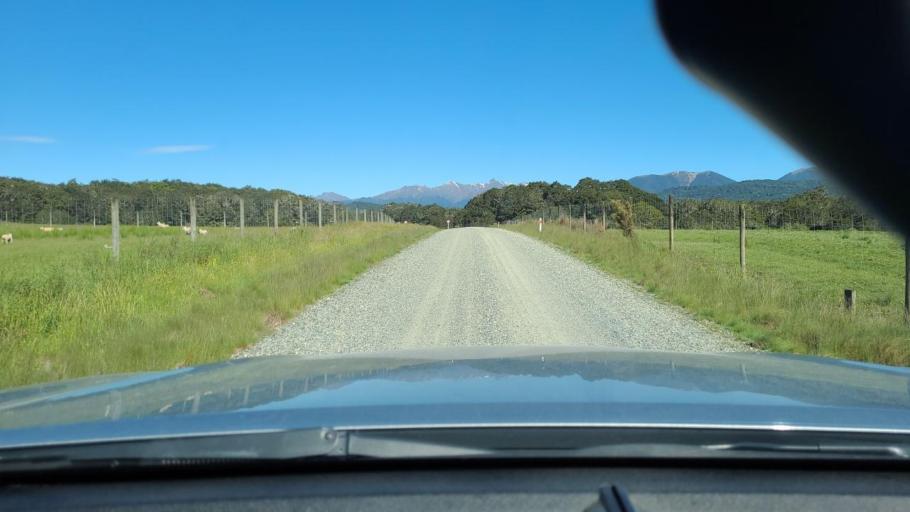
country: NZ
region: Southland
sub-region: Southland District
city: Te Anau
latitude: -46.0083
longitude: 167.4745
